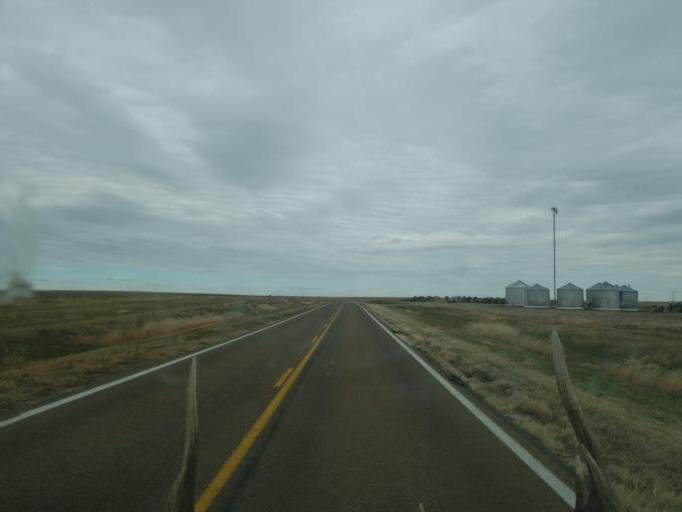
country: US
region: Kansas
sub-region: Wallace County
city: Sharon Springs
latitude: 38.9626
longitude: -101.4629
